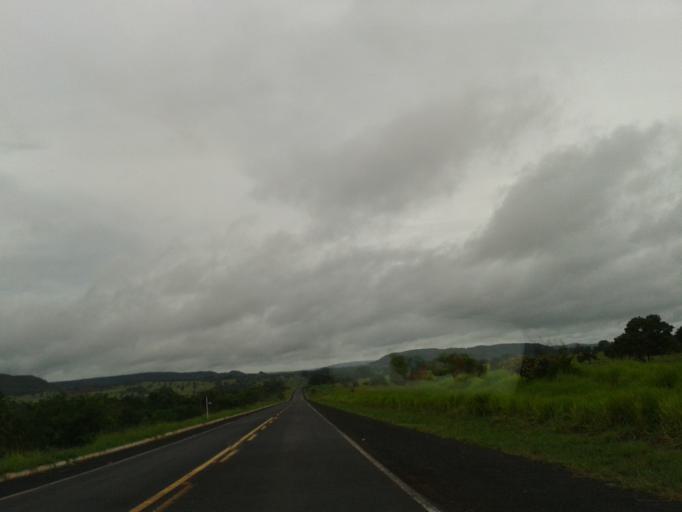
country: BR
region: Minas Gerais
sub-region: Santa Vitoria
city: Santa Vitoria
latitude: -19.2543
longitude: -50.0105
